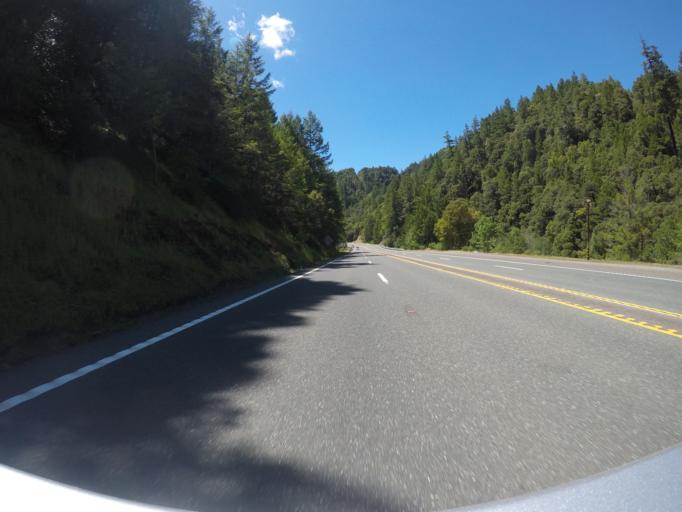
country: US
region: California
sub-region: Mendocino County
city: Laytonville
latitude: 39.8312
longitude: -123.6178
